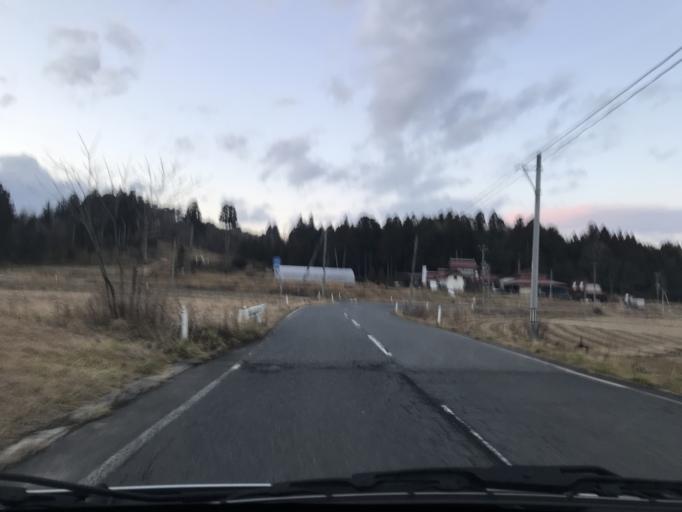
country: JP
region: Iwate
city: Ichinoseki
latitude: 38.8251
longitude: 141.1180
